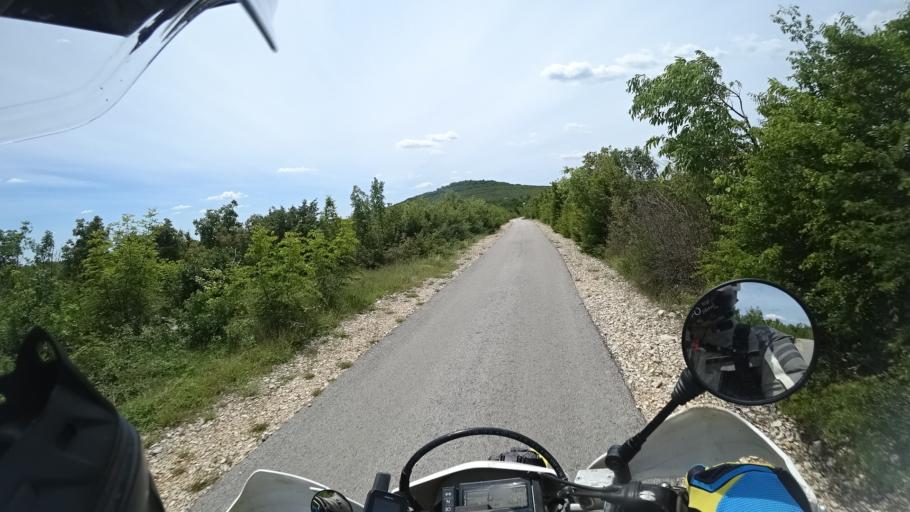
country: HR
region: Sibensko-Kniniska
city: Kistanje
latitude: 44.0594
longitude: 16.0413
